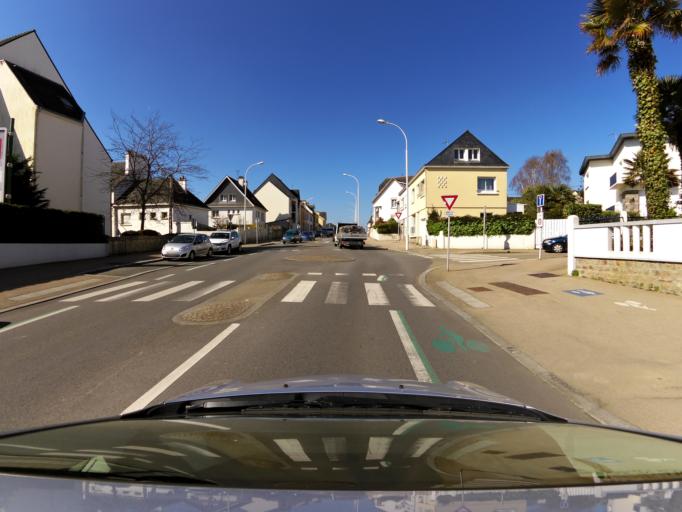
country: FR
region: Brittany
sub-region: Departement du Morbihan
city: Lorient
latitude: 47.7469
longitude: -3.3774
